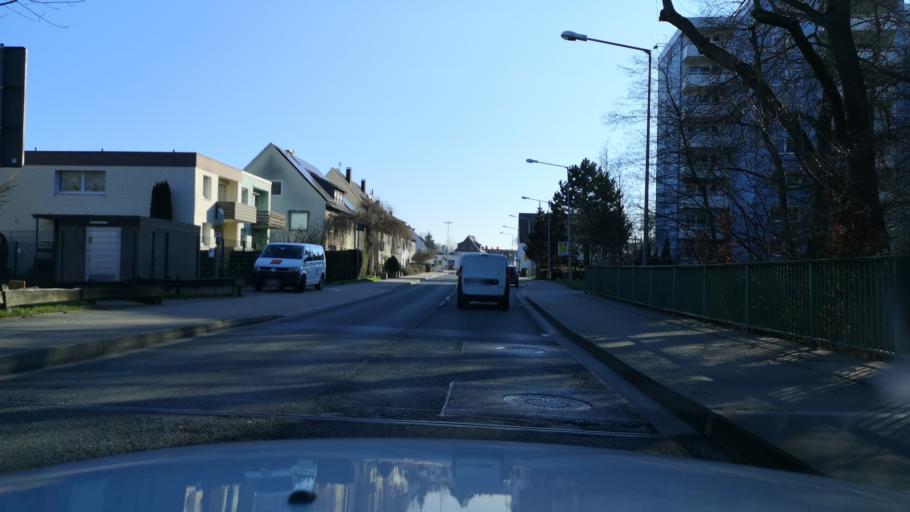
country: DE
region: North Rhine-Westphalia
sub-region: Regierungsbezirk Arnsberg
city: Menden
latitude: 51.4106
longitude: 7.8314
